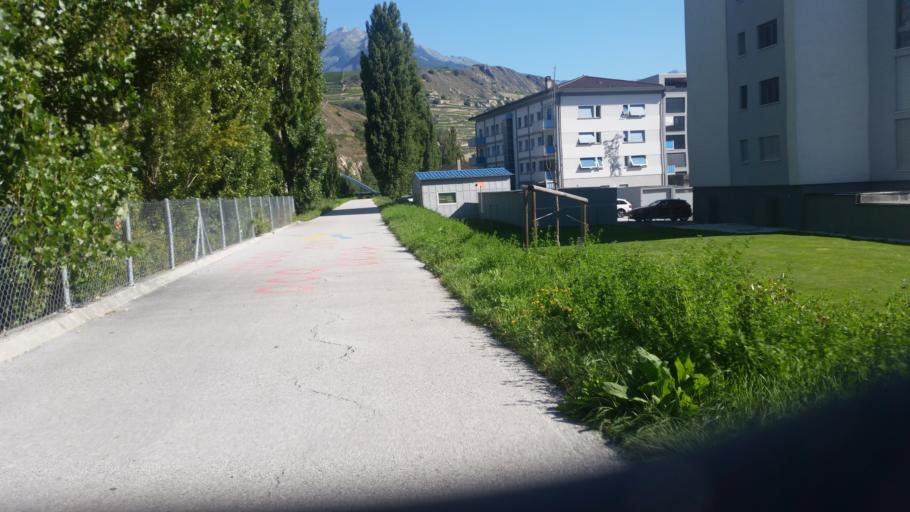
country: CH
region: Valais
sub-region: Sion District
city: Sitten
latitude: 46.2309
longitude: 7.3704
